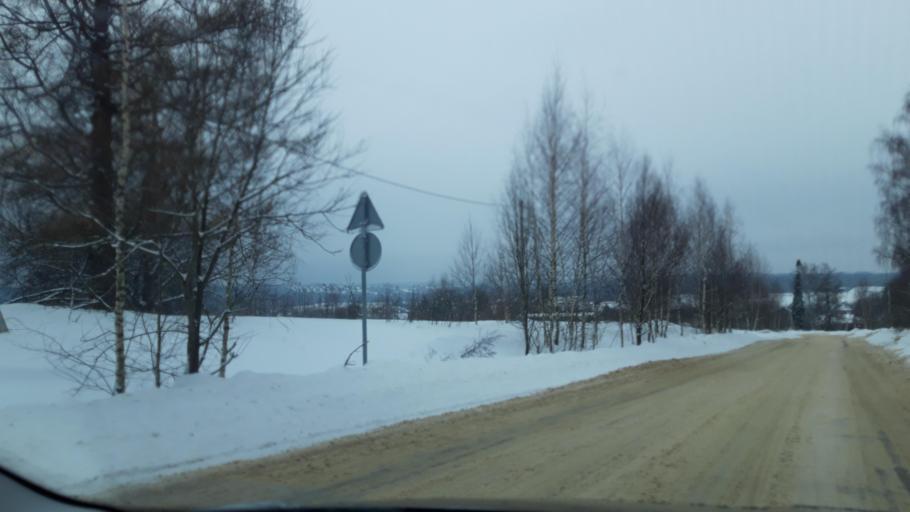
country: RU
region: Moskovskaya
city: Avtopoligon
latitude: 56.2587
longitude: 37.2439
